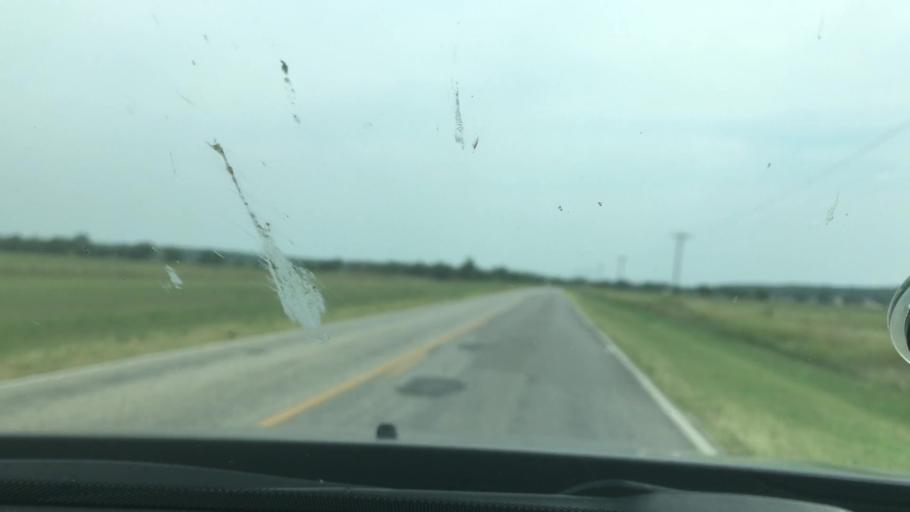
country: US
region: Oklahoma
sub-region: Johnston County
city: Tishomingo
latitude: 34.3410
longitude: -96.4217
